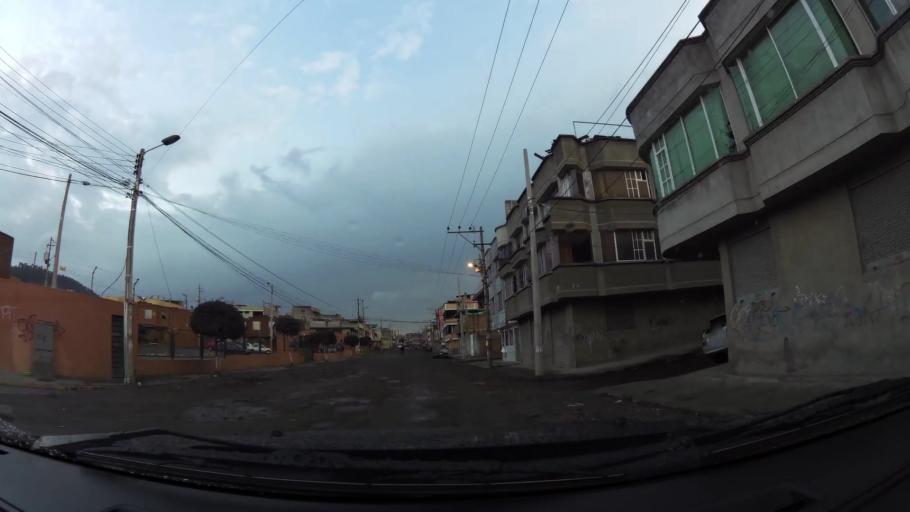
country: EC
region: Pichincha
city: Quito
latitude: -0.3020
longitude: -78.5389
